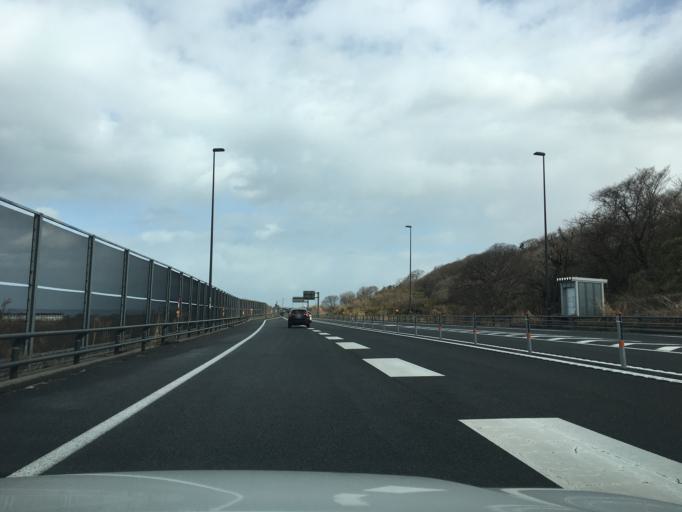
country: JP
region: Yamagata
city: Yuza
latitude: 39.2972
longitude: 139.9767
